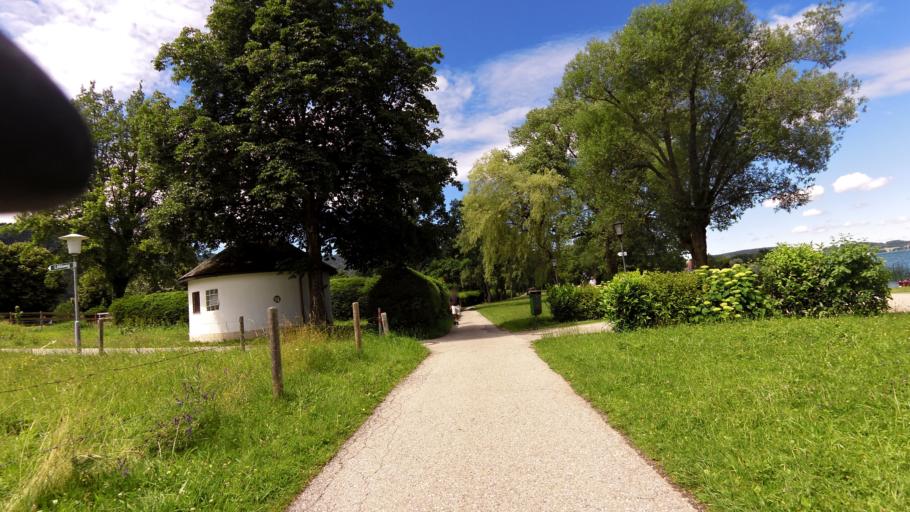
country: DE
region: Bavaria
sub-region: Upper Bavaria
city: Bad Wiessee
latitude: 47.7103
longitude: 11.7308
